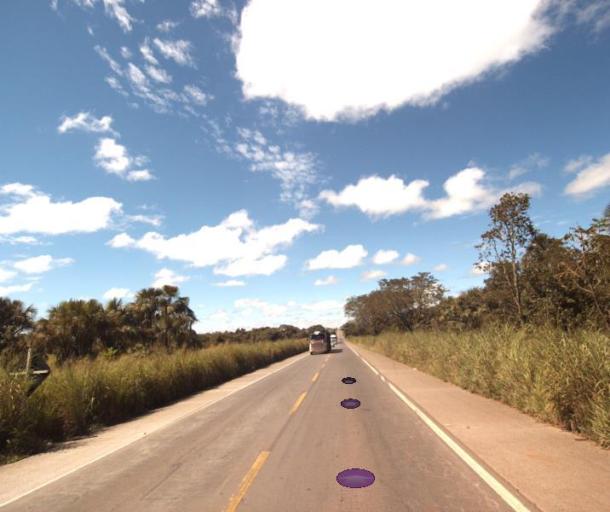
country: BR
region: Goias
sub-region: Rialma
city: Rialma
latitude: -15.4333
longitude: -49.5112
